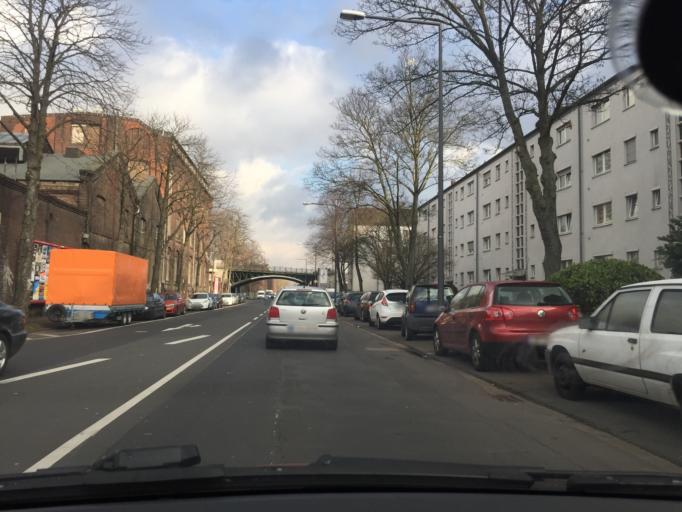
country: DE
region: North Rhine-Westphalia
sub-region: Regierungsbezirk Koln
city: Buchforst
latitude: 50.9509
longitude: 6.9886
